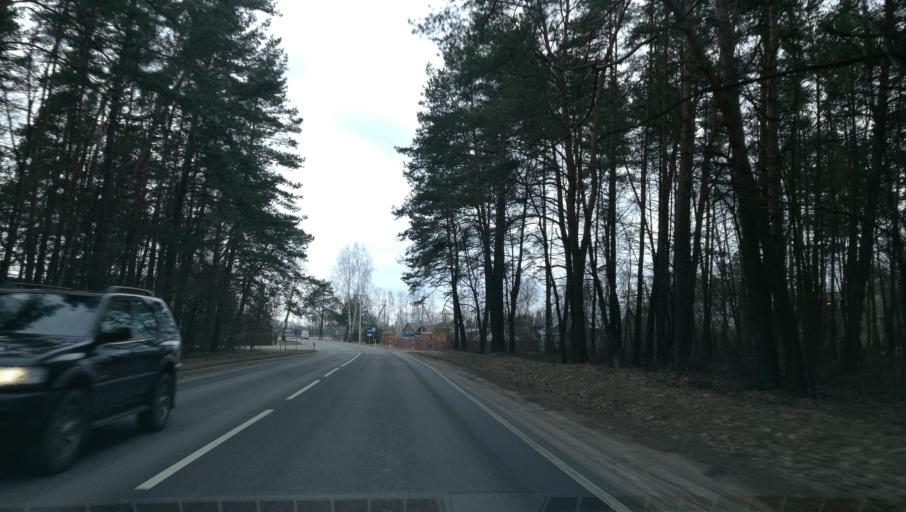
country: LT
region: Vilnius County
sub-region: Vilniaus Rajonas
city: Vievis
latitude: 54.7662
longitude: 24.8380
